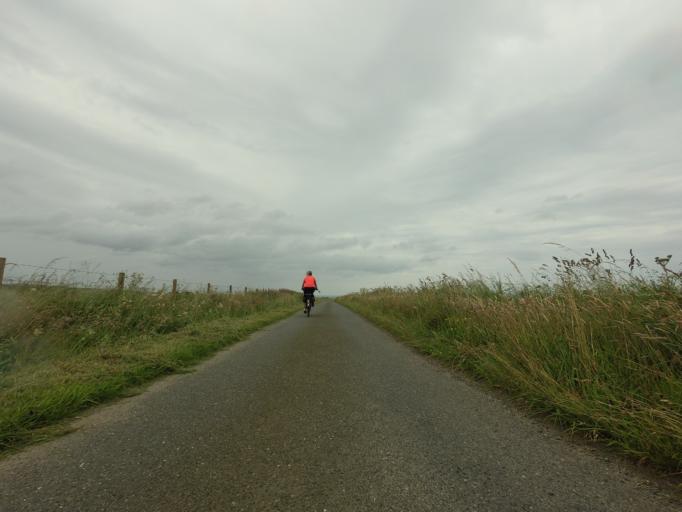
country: GB
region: Scotland
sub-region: Moray
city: Cullen
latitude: 57.6644
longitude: -2.7618
